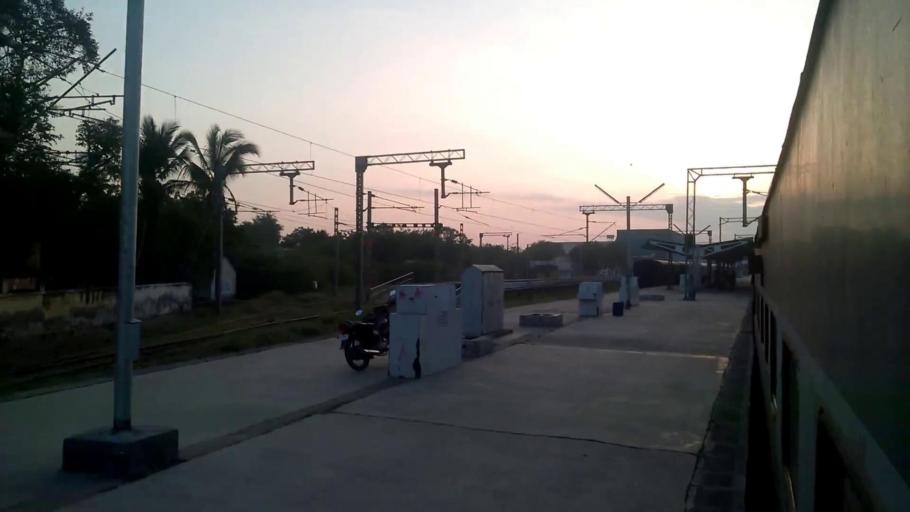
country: IN
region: Tamil Nadu
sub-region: Thoothukkudi
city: Korampallam
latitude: 8.8070
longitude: 78.1514
